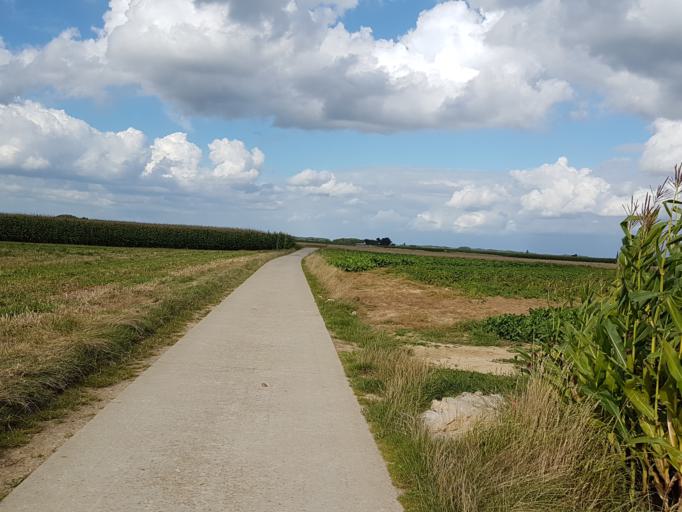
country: BE
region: Flanders
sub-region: Provincie Vlaams-Brabant
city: Kortenberg
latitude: 50.9108
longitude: 4.5364
